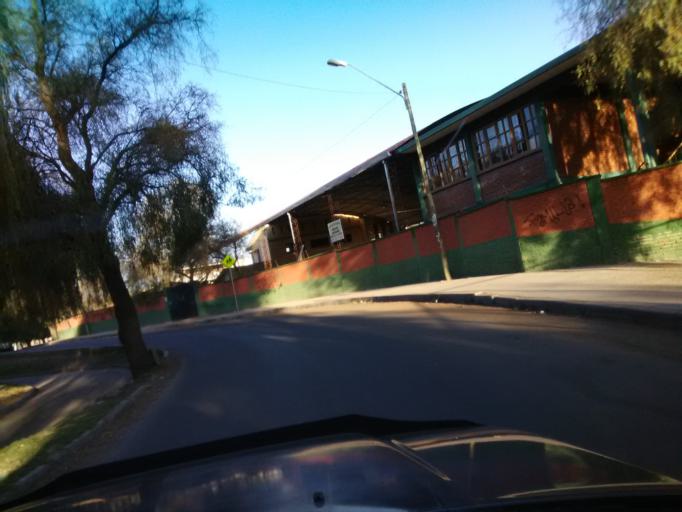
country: BO
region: Cochabamba
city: Cochabamba
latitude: -17.3677
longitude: -66.1615
